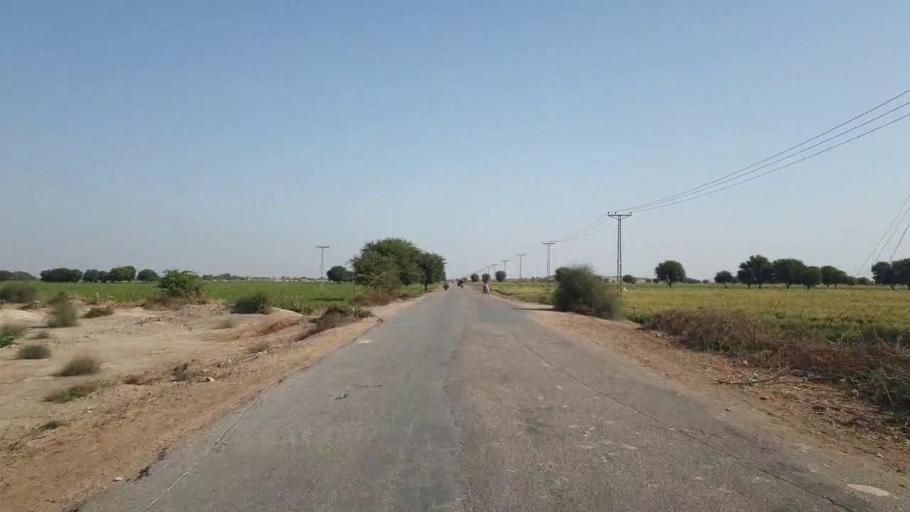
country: PK
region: Sindh
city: Umarkot
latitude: 25.4146
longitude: 69.7313
